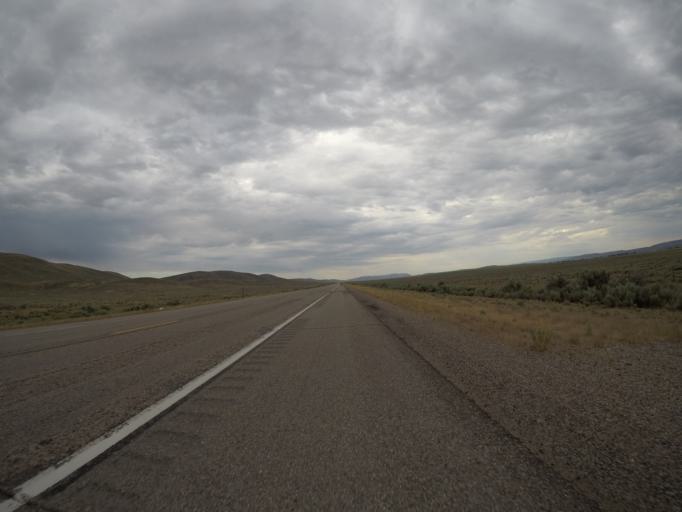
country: US
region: Utah
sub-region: Rich County
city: Randolph
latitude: 41.8870
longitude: -110.9626
